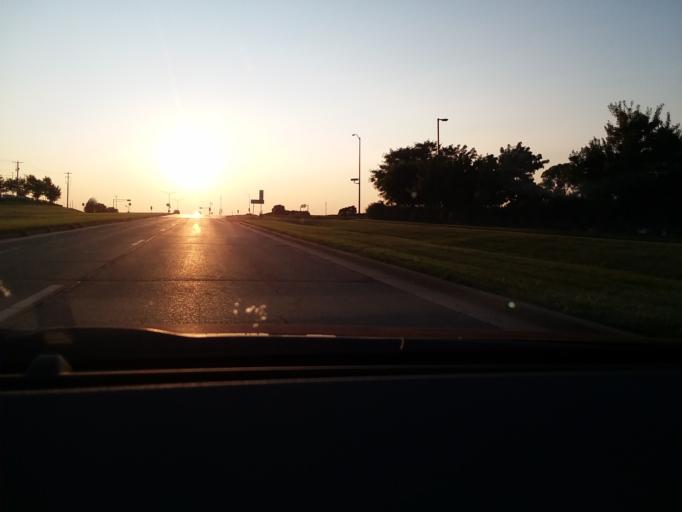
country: US
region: Wisconsin
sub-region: Dane County
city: Sun Prairie
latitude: 43.1437
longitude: -89.2797
